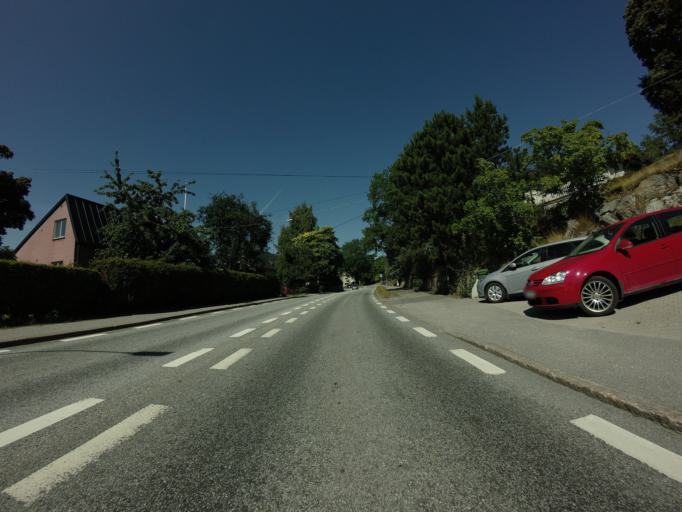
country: SE
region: Stockholm
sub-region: Lidingo
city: Brevik
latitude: 59.3422
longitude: 18.1759
